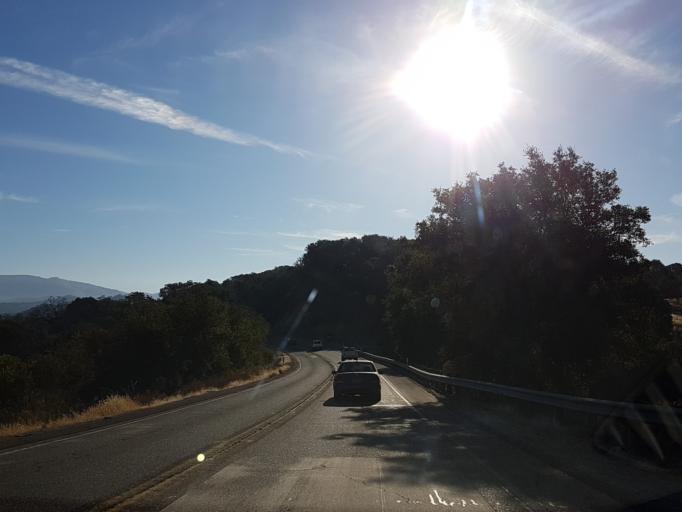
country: US
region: California
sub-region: Santa Barbara County
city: Goleta
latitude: 34.5617
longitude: -119.9267
